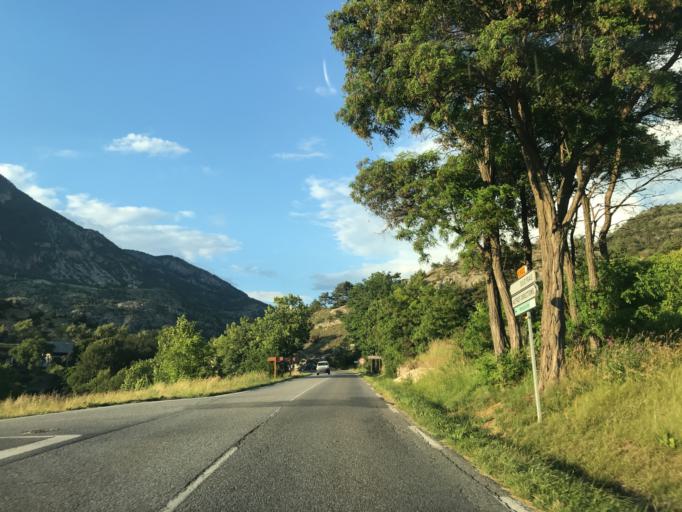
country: FR
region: Provence-Alpes-Cote d'Azur
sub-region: Departement des Hautes-Alpes
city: Guillestre
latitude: 44.6614
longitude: 6.6599
